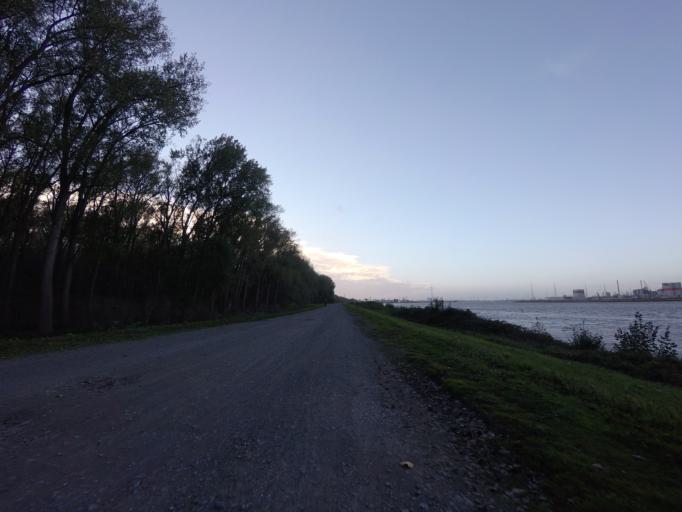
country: BE
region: Flanders
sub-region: Provincie Antwerpen
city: Antwerpen
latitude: 51.2361
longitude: 4.3711
